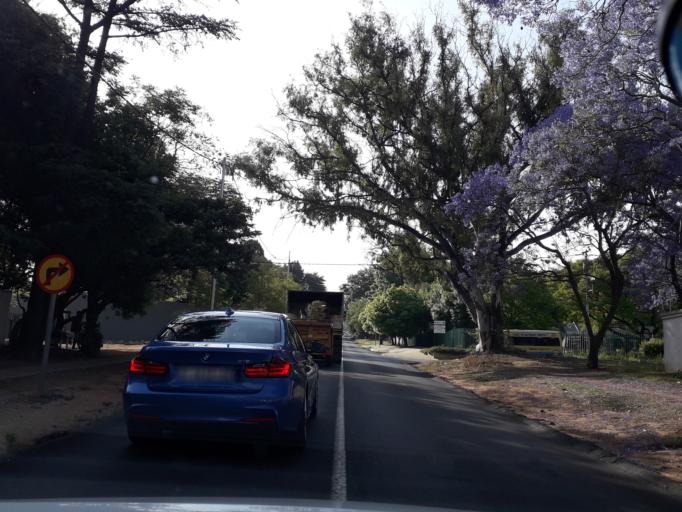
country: ZA
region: Gauteng
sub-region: City of Johannesburg Metropolitan Municipality
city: Midrand
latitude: -26.0659
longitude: 28.0325
